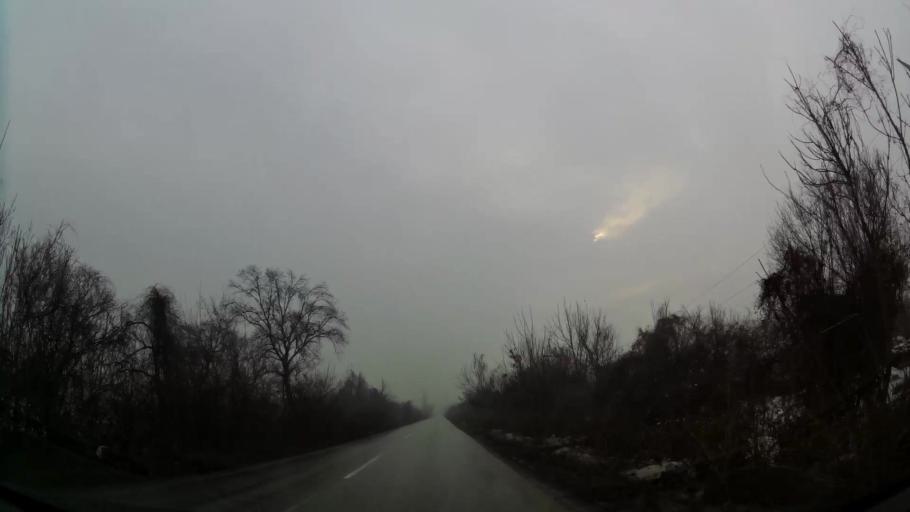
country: MK
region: Ilinden
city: Idrizovo
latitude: 41.9523
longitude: 21.5819
